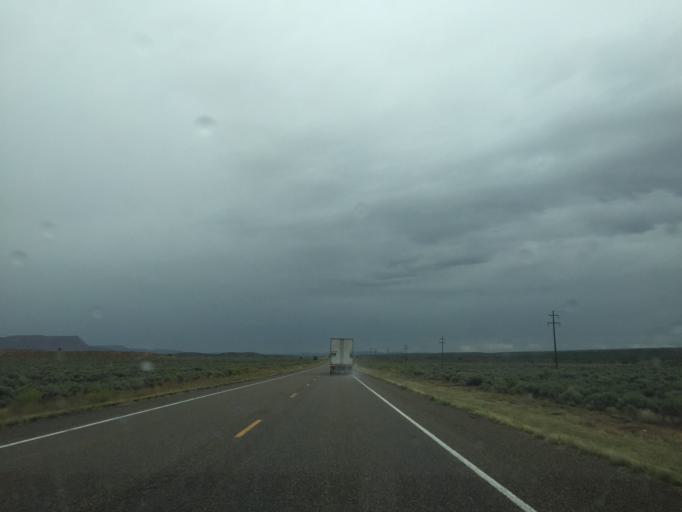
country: US
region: Utah
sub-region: Kane County
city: Kanab
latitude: 37.1158
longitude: -112.1104
